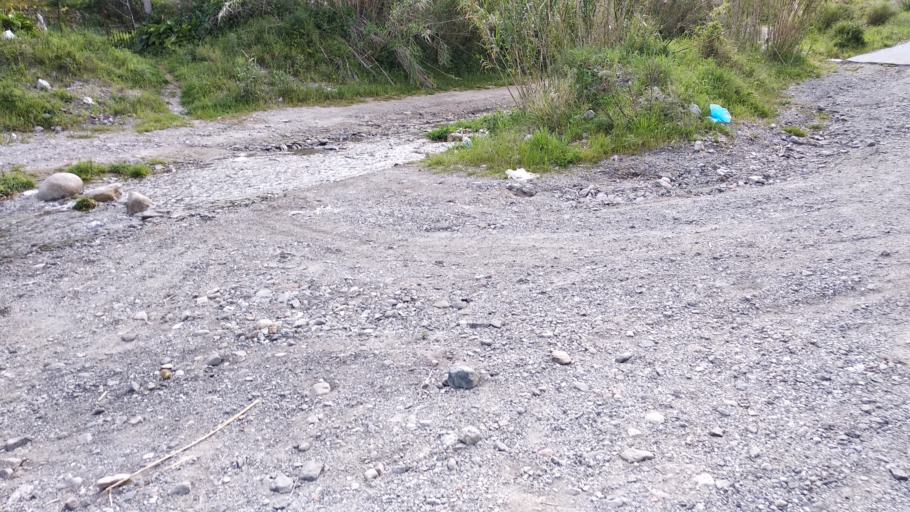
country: IT
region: Sicily
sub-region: Messina
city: Villafranca Tirrena
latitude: 38.2243
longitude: 15.4512
